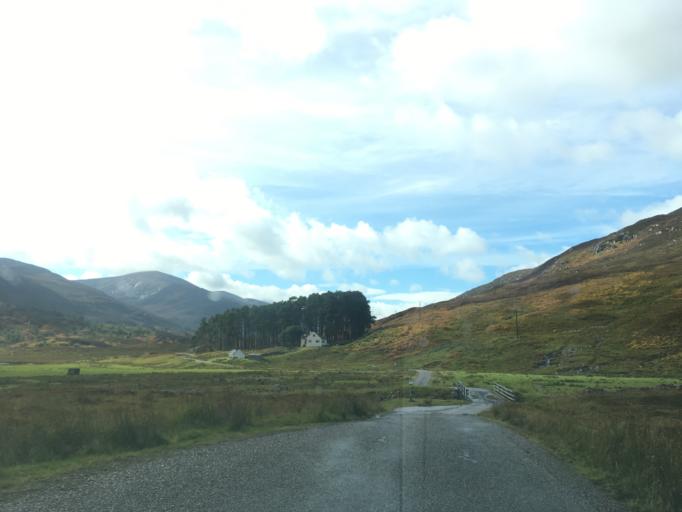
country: GB
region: Scotland
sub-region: Highland
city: Spean Bridge
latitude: 57.3513
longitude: -4.9068
